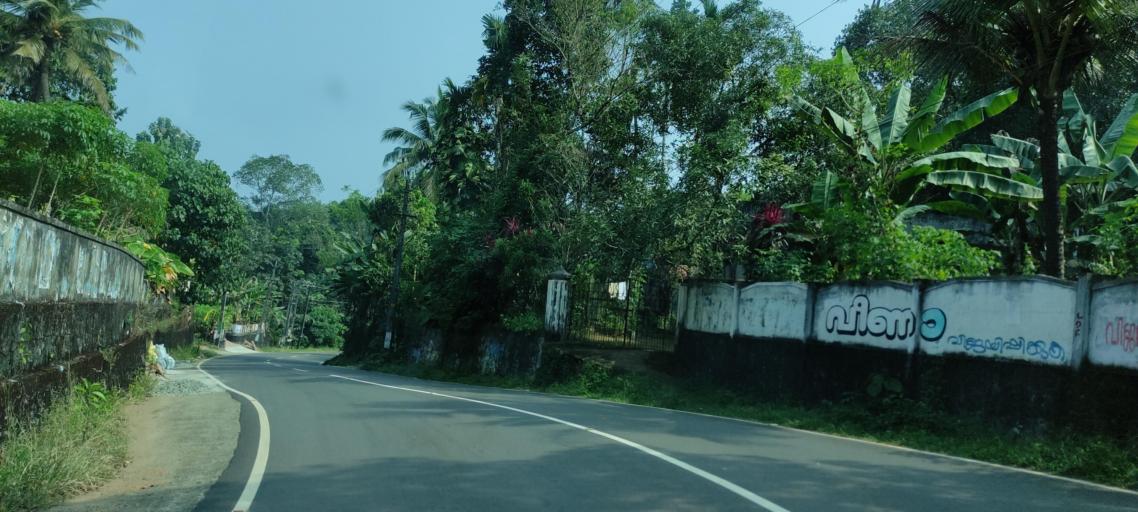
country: IN
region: Kerala
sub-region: Pattanamtitta
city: Adur
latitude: 9.2401
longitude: 76.6833
